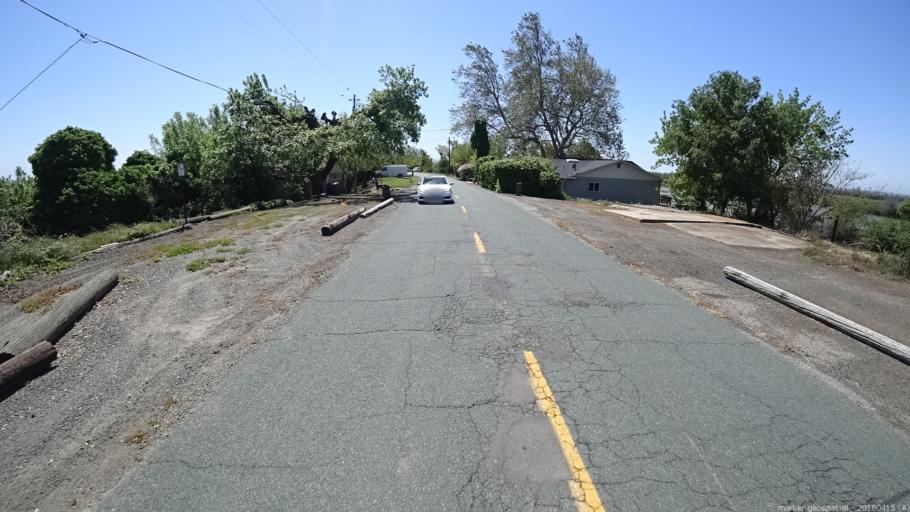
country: US
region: California
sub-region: Solano County
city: Rio Vista
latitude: 38.2078
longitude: -121.6093
